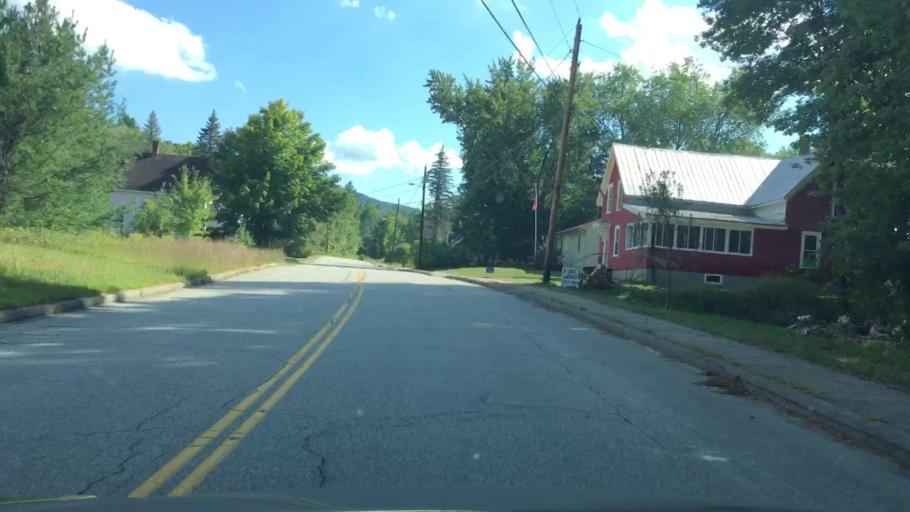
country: US
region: New Hampshire
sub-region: Carroll County
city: North Conway
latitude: 44.0736
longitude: -71.2832
